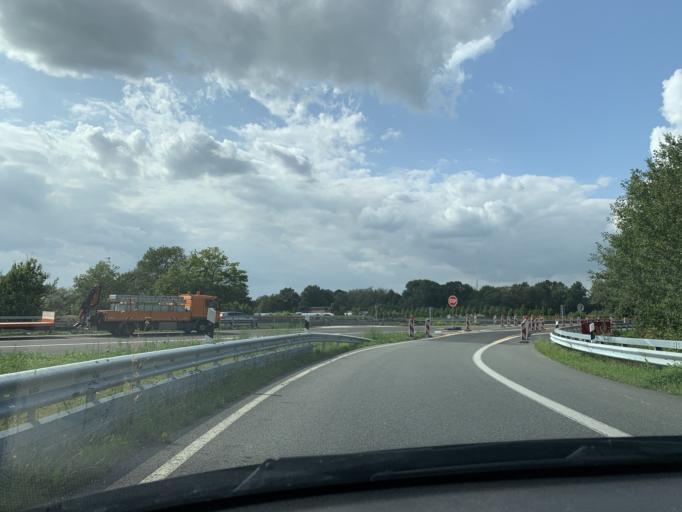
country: DE
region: Lower Saxony
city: Wiefelstede
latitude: 53.1909
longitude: 8.1025
